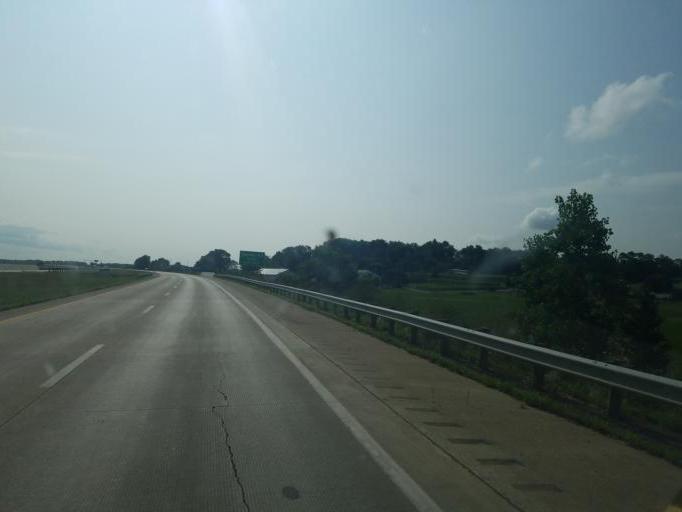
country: US
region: Ohio
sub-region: Wayne County
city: Apple Creek
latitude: 40.7925
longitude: -81.8058
